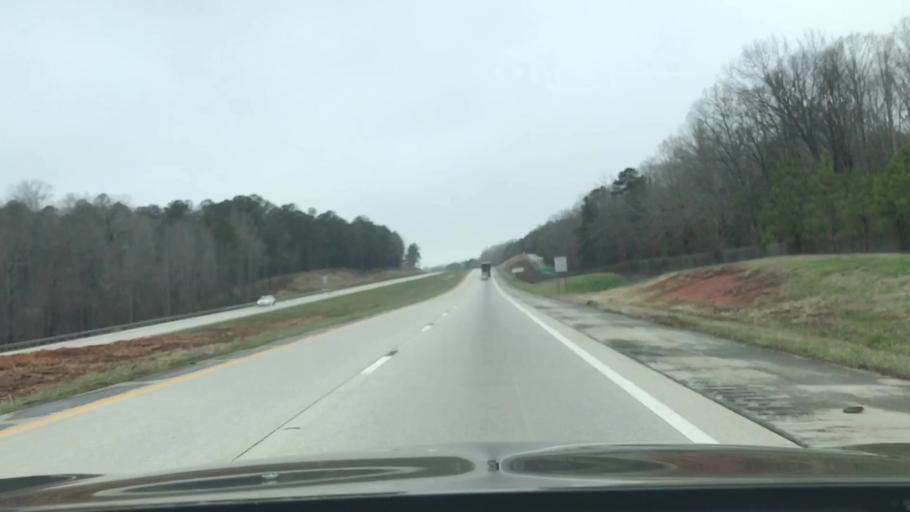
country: US
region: South Carolina
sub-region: Laurens County
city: Clinton
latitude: 34.5159
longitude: -81.8809
